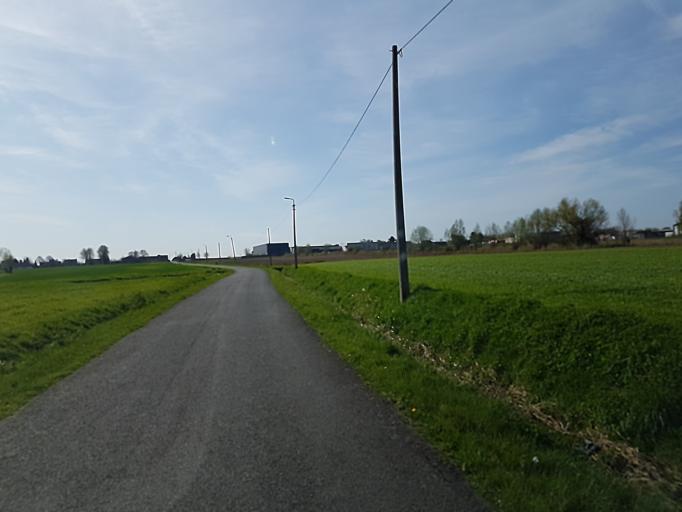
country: BE
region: Flanders
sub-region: Provincie West-Vlaanderen
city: Waregem
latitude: 50.8493
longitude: 3.4277
